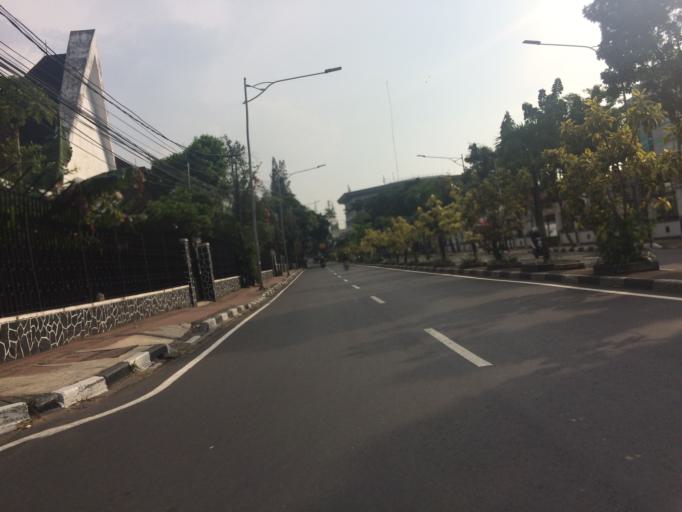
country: ID
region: Jakarta Raya
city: Jakarta
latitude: -6.1671
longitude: 106.8380
